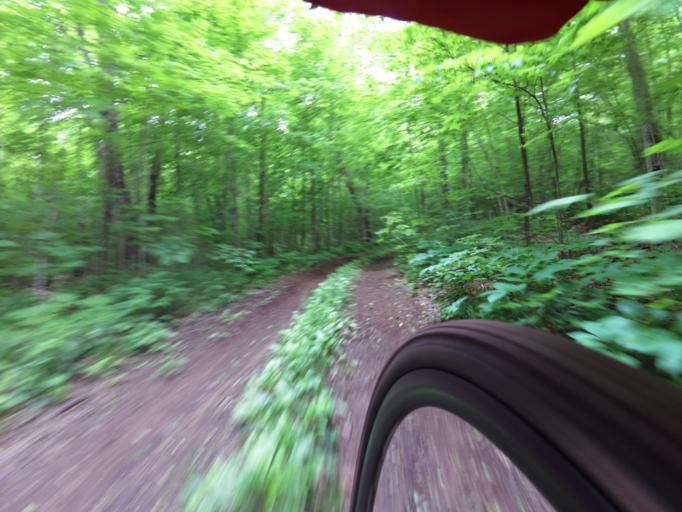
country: CA
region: Ontario
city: Arnprior
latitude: 45.1827
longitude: -76.5323
